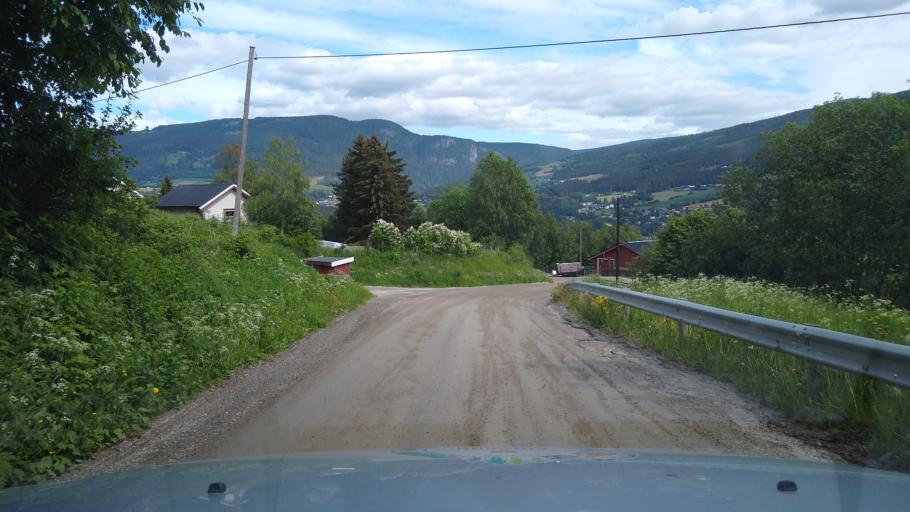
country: NO
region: Oppland
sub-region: Ringebu
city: Ringebu
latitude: 61.5167
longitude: 10.1321
